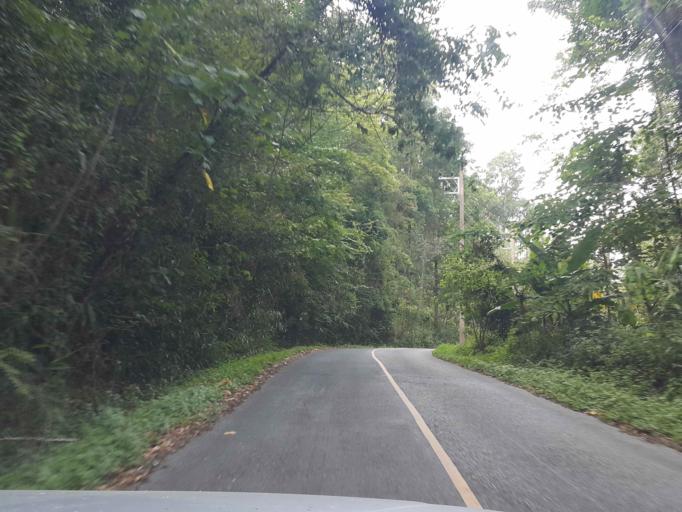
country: TH
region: Chiang Mai
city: Mae On
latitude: 18.9409
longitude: 99.3563
